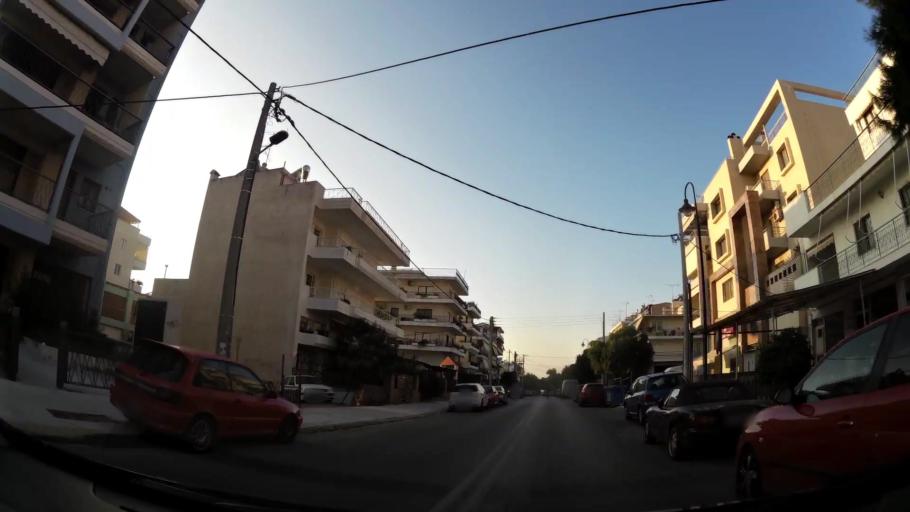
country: GR
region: Attica
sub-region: Nomarchia Athinas
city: Glyfada
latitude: 37.8866
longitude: 23.7715
